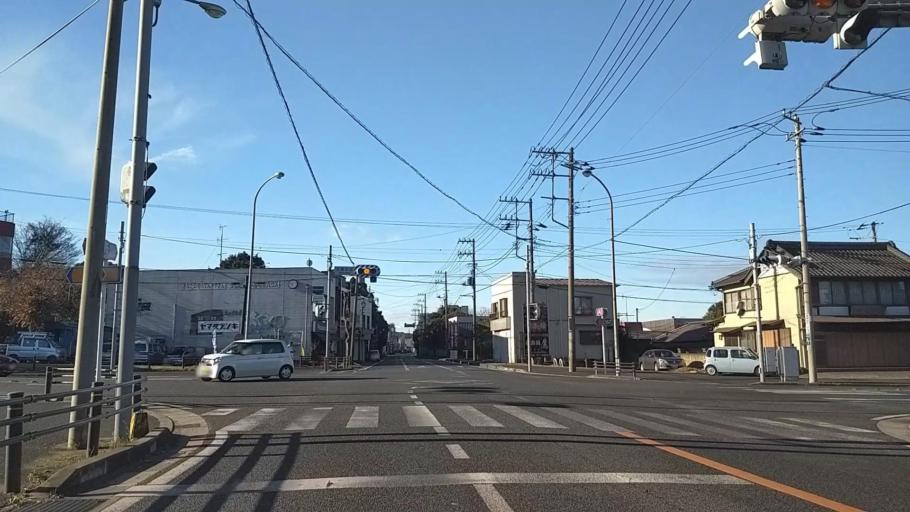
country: JP
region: Chiba
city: Kimitsu
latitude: 35.3343
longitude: 139.8627
